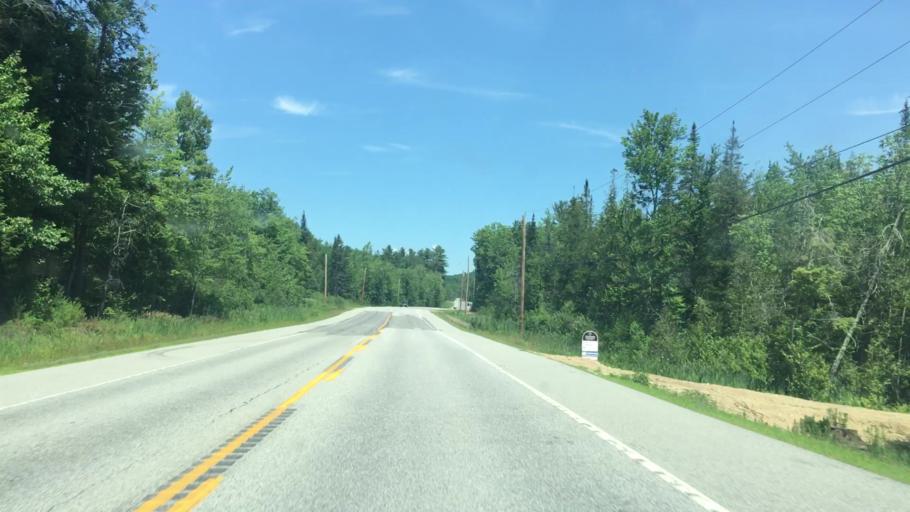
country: US
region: Maine
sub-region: Androscoggin County
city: Livermore
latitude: 44.4010
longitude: -70.2274
